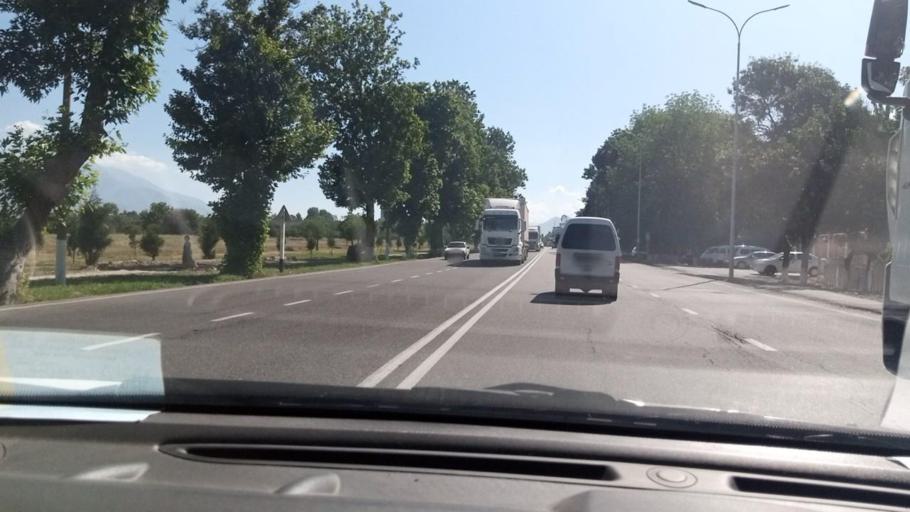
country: UZ
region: Toshkent
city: Angren
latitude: 40.9965
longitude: 70.0658
